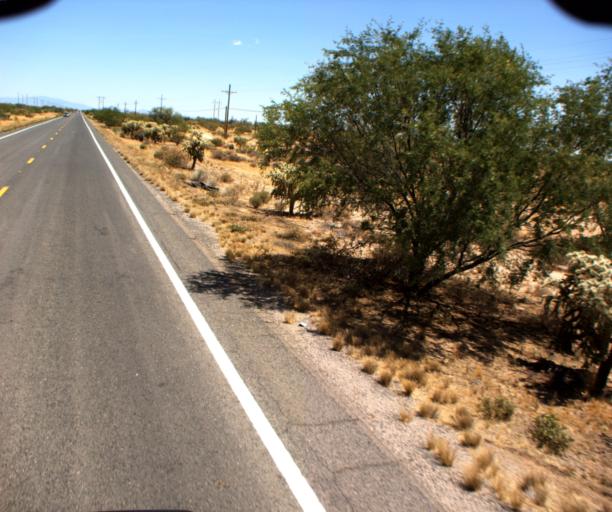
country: US
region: Arizona
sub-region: Pinal County
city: Florence
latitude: 32.9343
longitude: -111.3105
